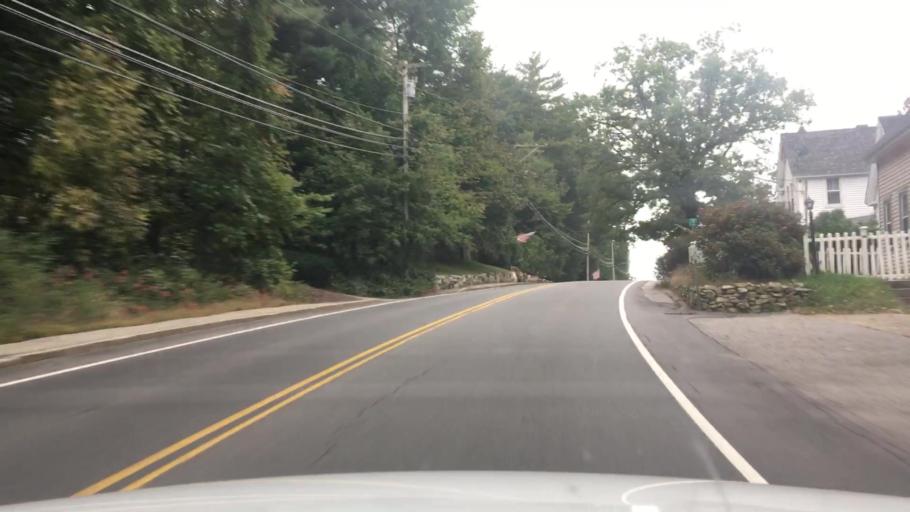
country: US
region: New Hampshire
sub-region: Strafford County
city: New Durham
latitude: 43.4628
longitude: -71.2276
